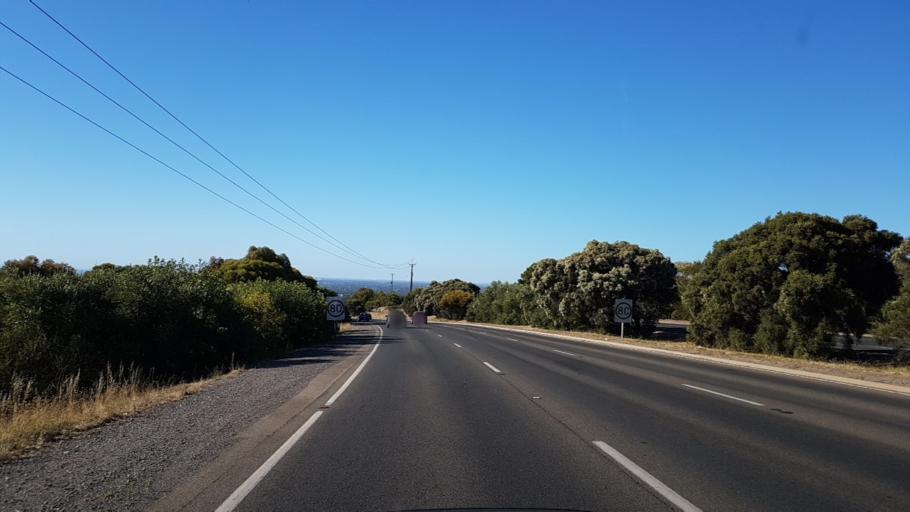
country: AU
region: South Australia
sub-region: Onkaparinga
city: Bedford Park
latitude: -35.0444
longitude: 138.5608
